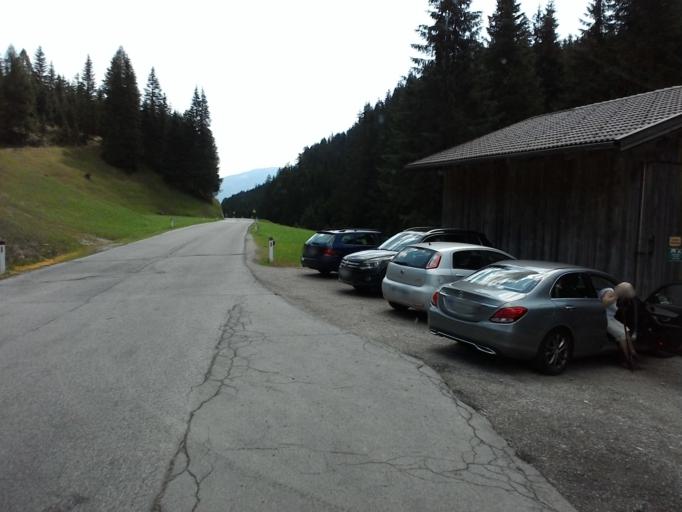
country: AT
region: Tyrol
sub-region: Politischer Bezirk Lienz
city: Abfaltersbach
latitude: 46.7174
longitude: 12.5435
